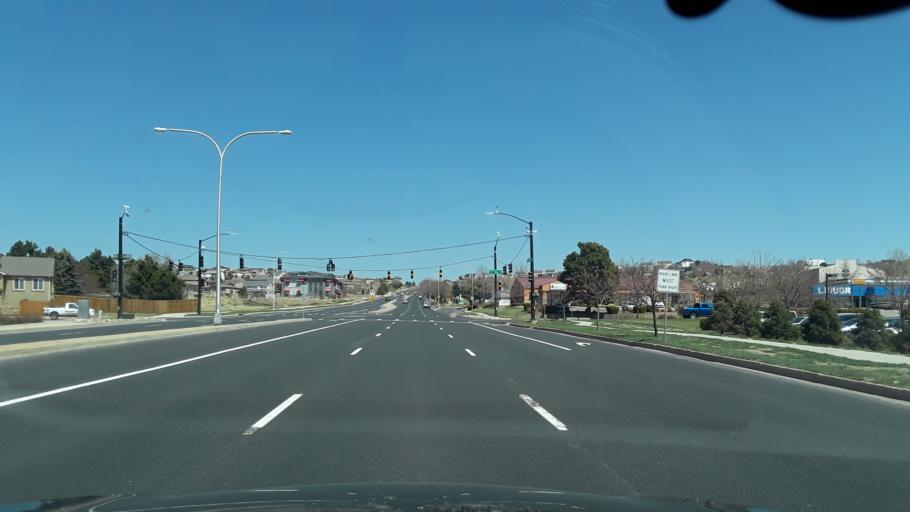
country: US
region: Colorado
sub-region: El Paso County
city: Cimarron Hills
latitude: 38.9050
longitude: -104.7386
